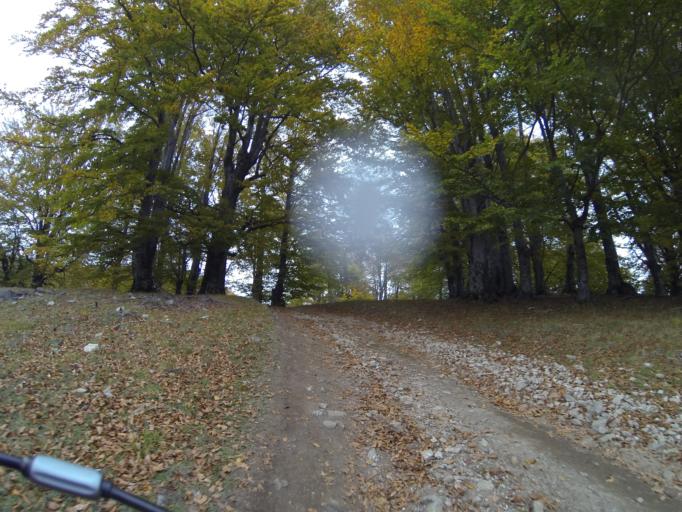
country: RO
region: Gorj
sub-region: Comuna Tismana
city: Sohodol
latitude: 45.1334
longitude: 22.8759
